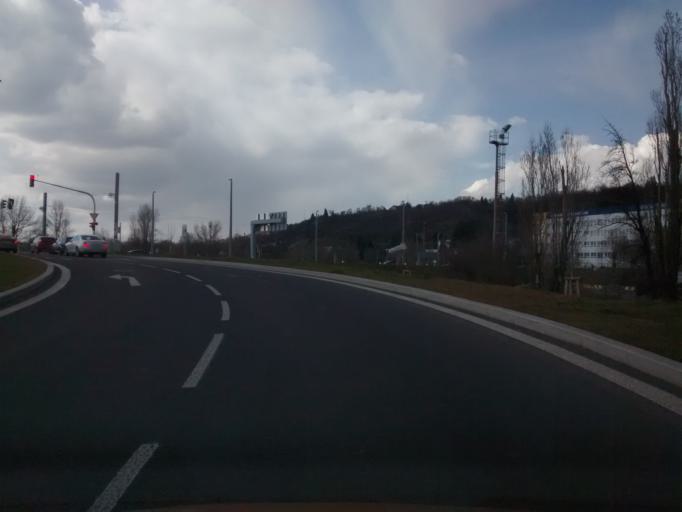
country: CZ
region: Praha
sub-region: Praha 8
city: Karlin
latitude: 50.1148
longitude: 14.4362
